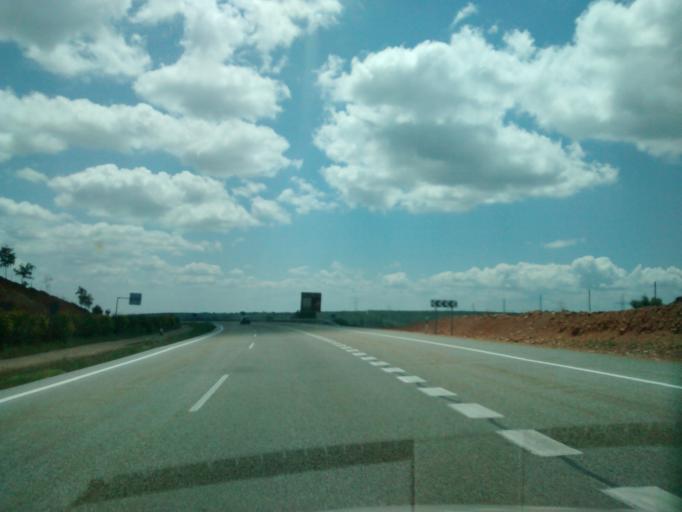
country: ES
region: Castille and Leon
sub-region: Provincia de Leon
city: Brazuelo
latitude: 42.4889
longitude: -6.1267
